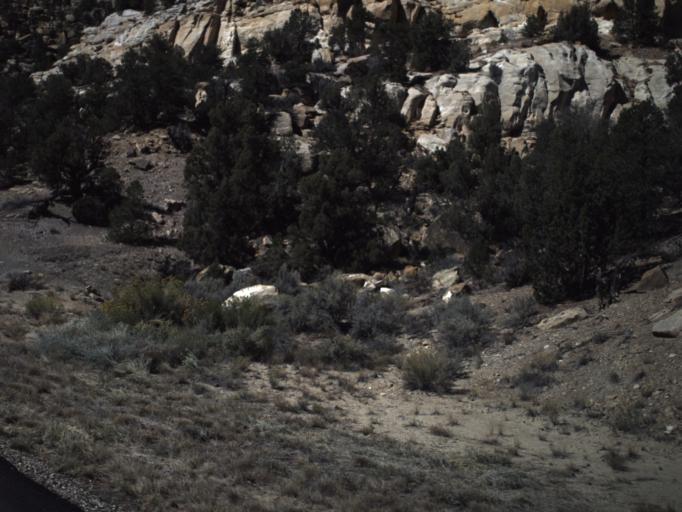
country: US
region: Utah
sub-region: Wayne County
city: Loa
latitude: 37.7422
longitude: -111.7213
